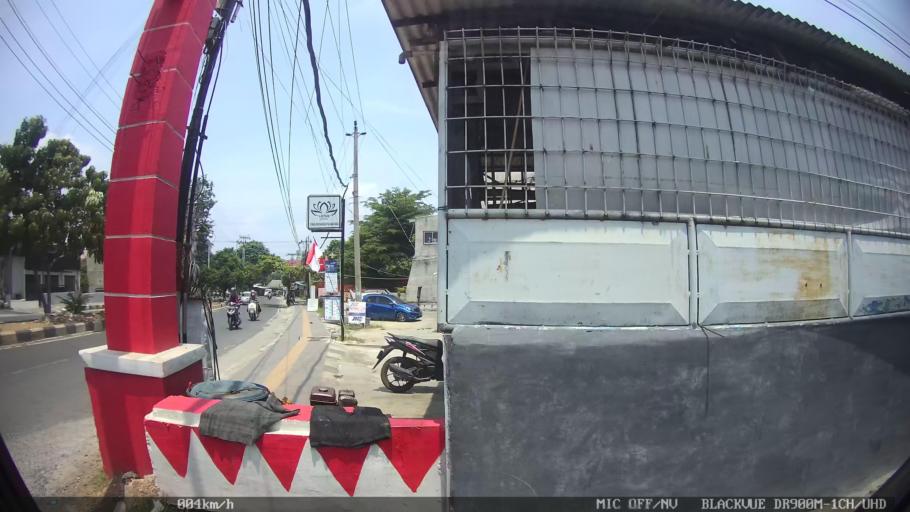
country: ID
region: Lampung
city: Bandarlampung
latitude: -5.4352
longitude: 105.2509
